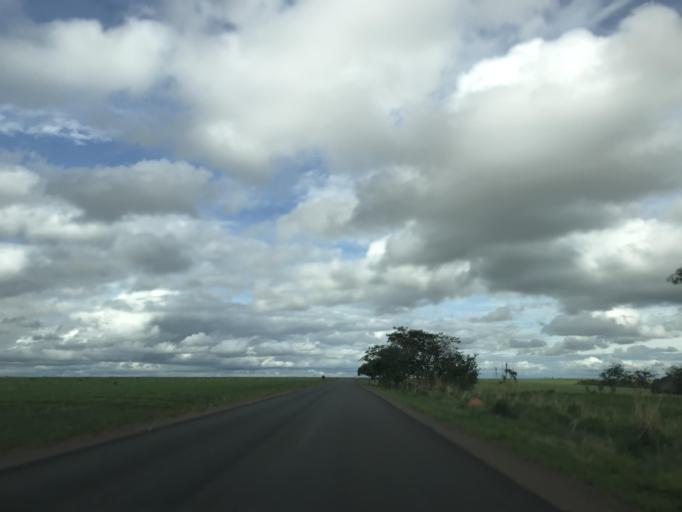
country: BR
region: Goias
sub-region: Vianopolis
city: Vianopolis
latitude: -16.9631
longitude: -48.6428
